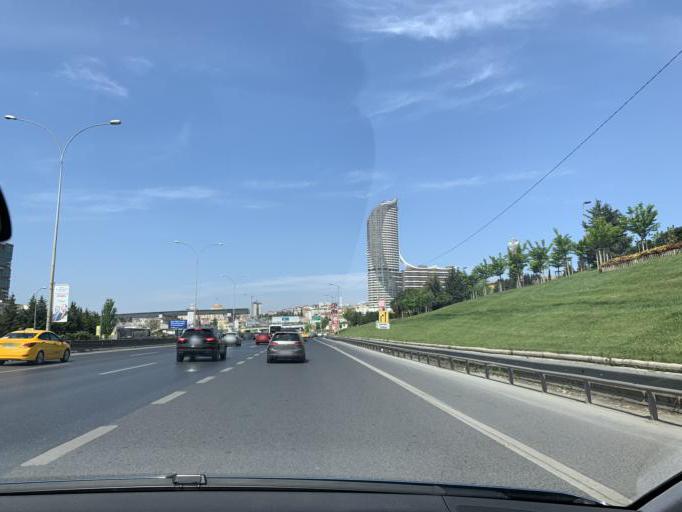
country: TR
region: Istanbul
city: UEskuedar
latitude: 40.9968
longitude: 29.0623
